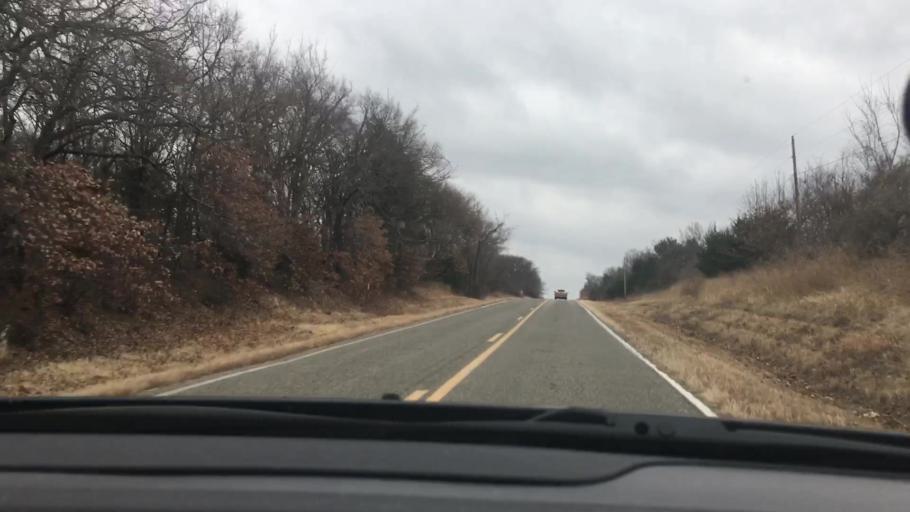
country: US
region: Oklahoma
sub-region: Johnston County
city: Tishomingo
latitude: 34.2087
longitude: -96.6139
